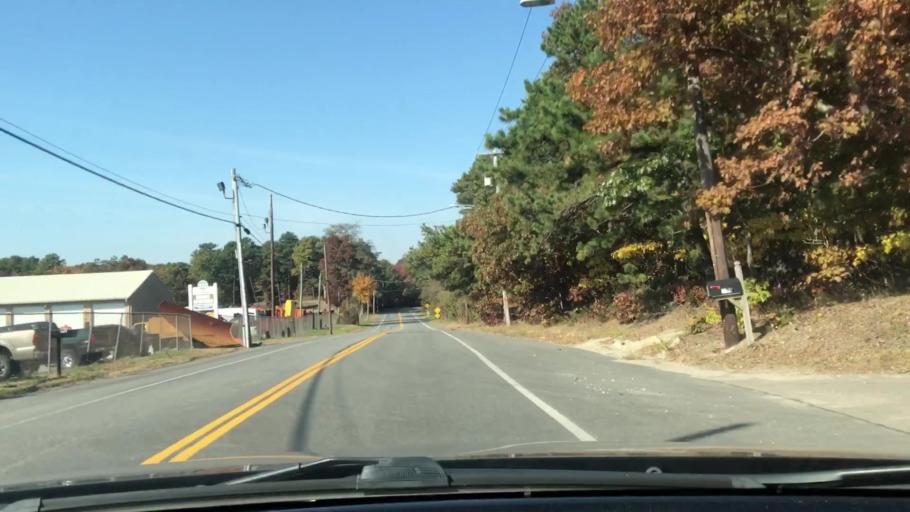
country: US
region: New York
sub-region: Suffolk County
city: Riverhead
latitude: 40.9294
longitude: -72.6885
